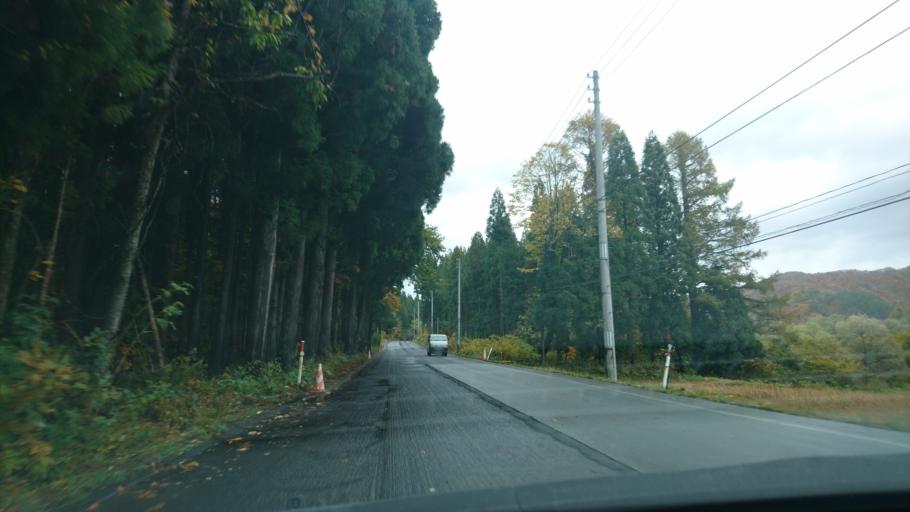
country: JP
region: Iwate
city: Shizukuishi
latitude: 39.4991
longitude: 140.8167
